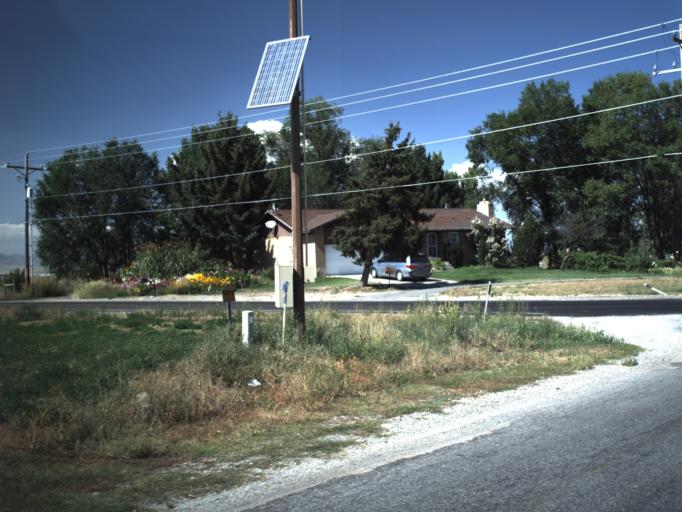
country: US
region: Utah
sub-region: Cache County
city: Lewiston
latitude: 41.9755
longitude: -111.8762
